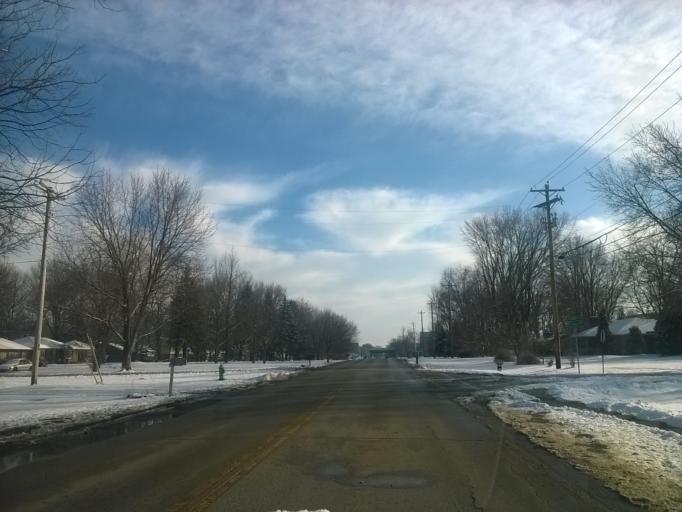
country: US
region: Indiana
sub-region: Marion County
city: Meridian Hills
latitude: 39.9348
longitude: -86.1460
